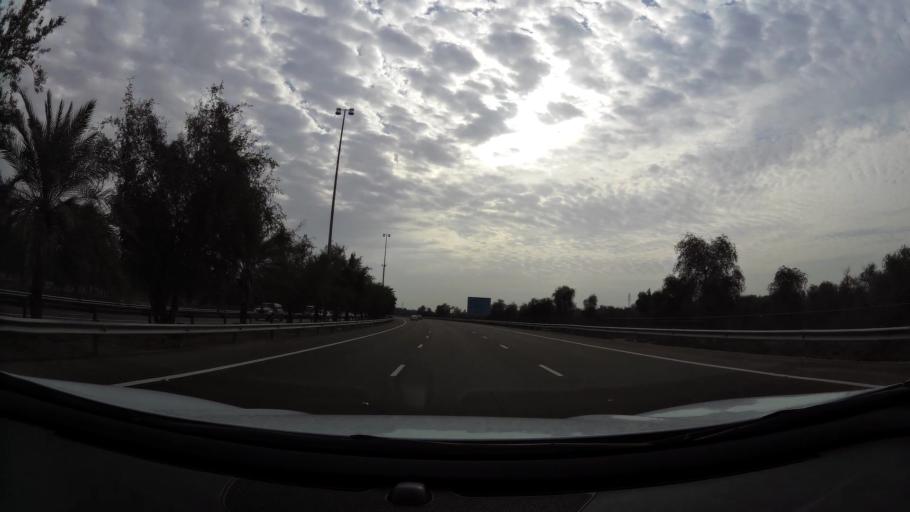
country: AE
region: Abu Dhabi
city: Al Ain
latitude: 24.1676
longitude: 55.2697
